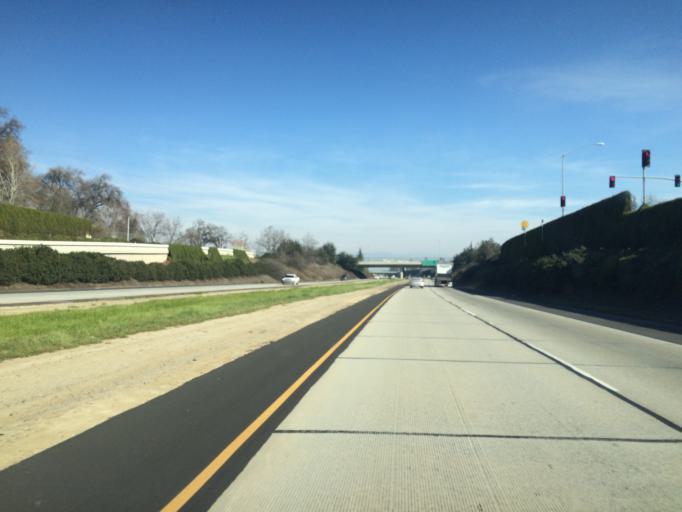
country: US
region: California
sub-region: Tulare County
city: Visalia
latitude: 36.3274
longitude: -119.3351
